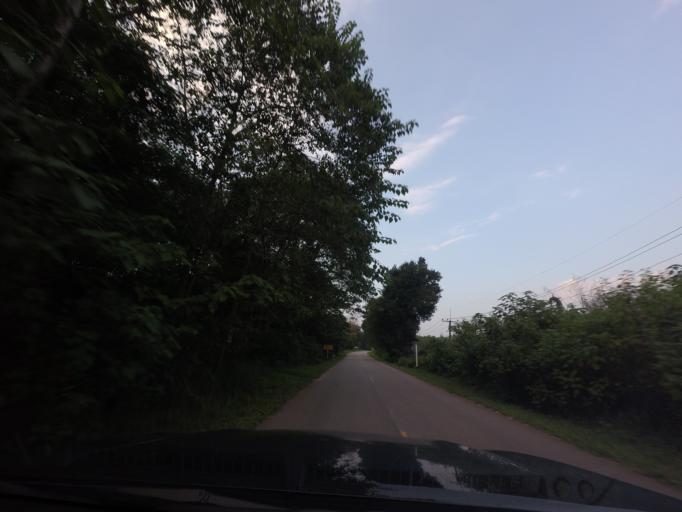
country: TH
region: Loei
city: Na Haeo
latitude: 17.4189
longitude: 101.0478
